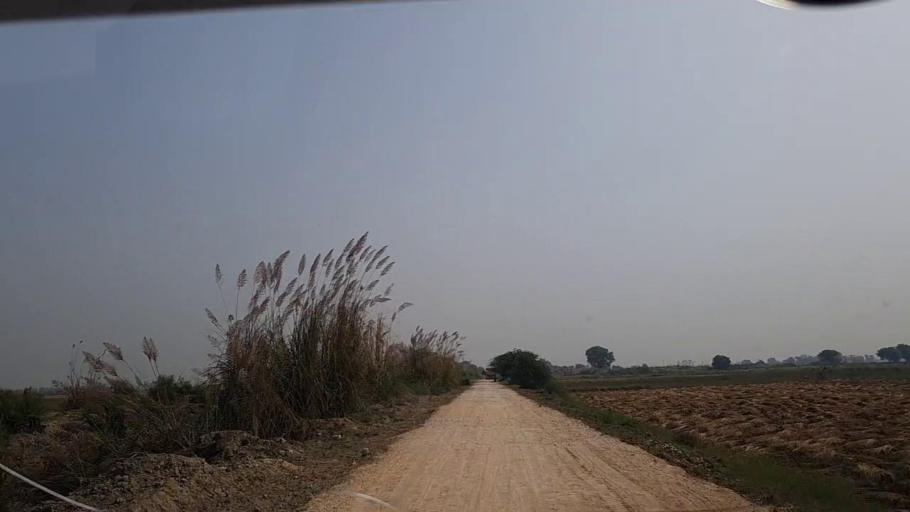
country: PK
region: Sindh
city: Garhi Yasin
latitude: 27.9210
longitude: 68.5770
